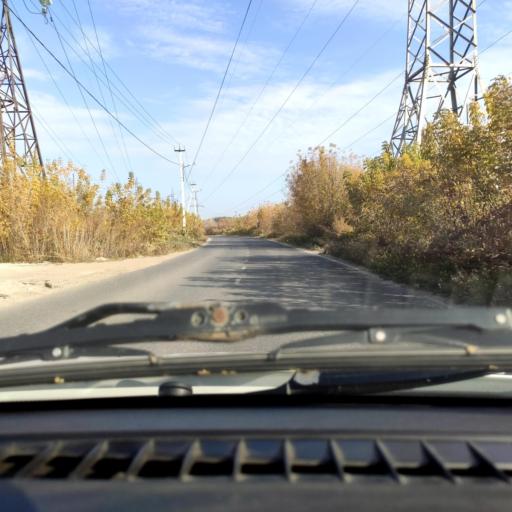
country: RU
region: Samara
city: Zhigulevsk
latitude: 53.5199
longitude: 49.4851
